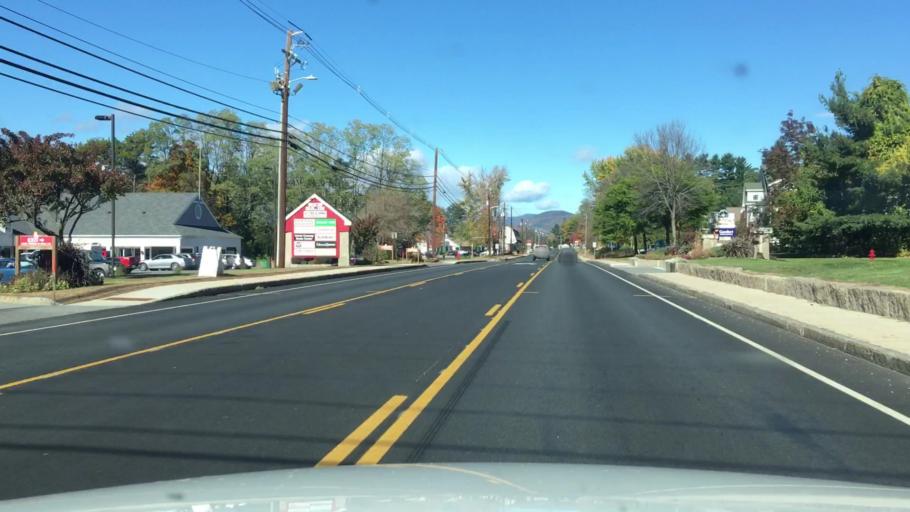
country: US
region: New Hampshire
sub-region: Carroll County
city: North Conway
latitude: 44.0331
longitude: -71.1209
